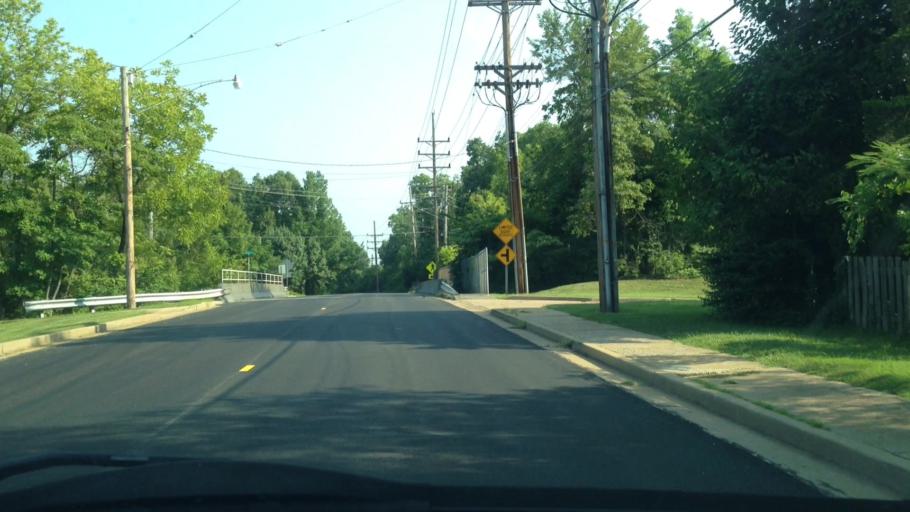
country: US
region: Missouri
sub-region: Saint Louis County
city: Des Peres
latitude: 38.5759
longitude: -90.4348
